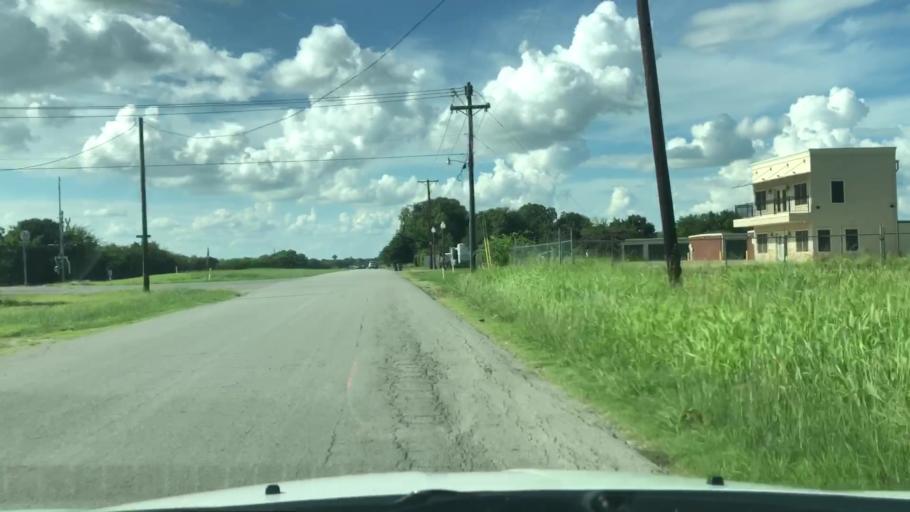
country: US
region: Texas
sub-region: Ellis County
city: Ennis
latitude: 32.3509
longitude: -96.6421
